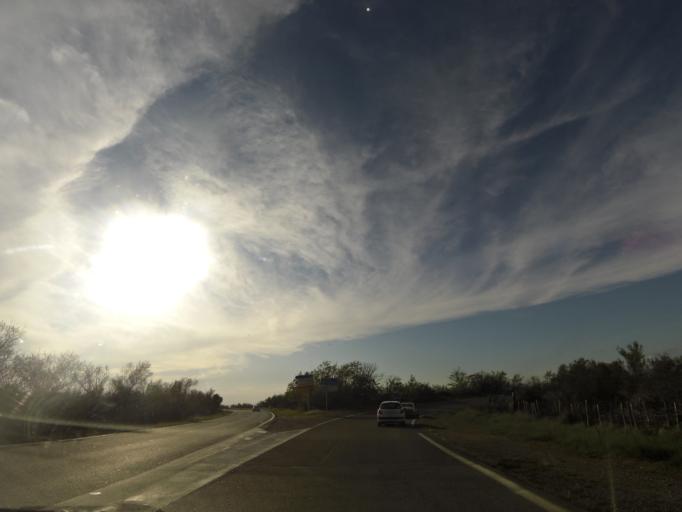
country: FR
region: Languedoc-Roussillon
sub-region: Departement de l'Herault
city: La Grande-Motte
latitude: 43.5779
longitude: 4.1014
